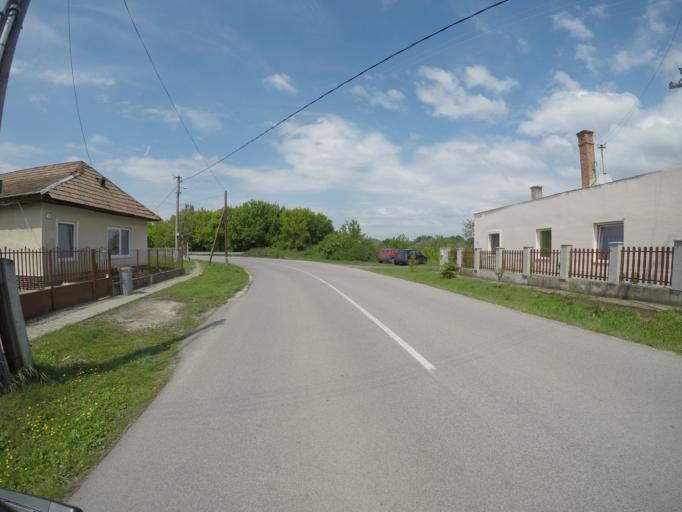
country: SK
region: Nitriansky
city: Zeliezovce
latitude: 47.9720
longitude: 18.7536
